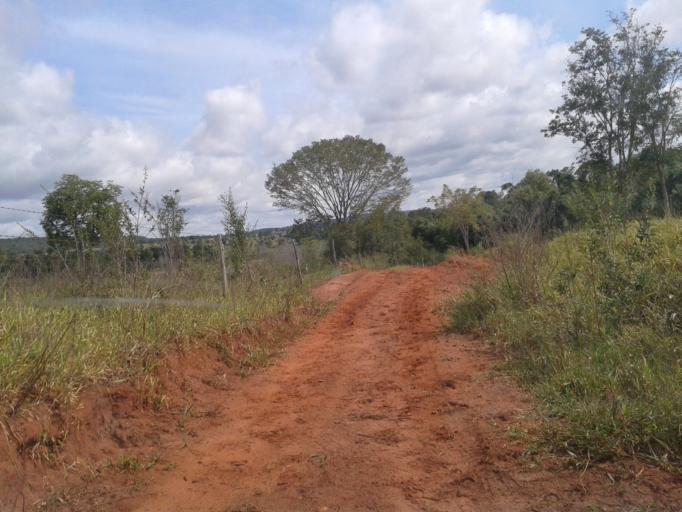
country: BR
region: Minas Gerais
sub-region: Campina Verde
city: Campina Verde
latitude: -19.4285
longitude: -49.6934
